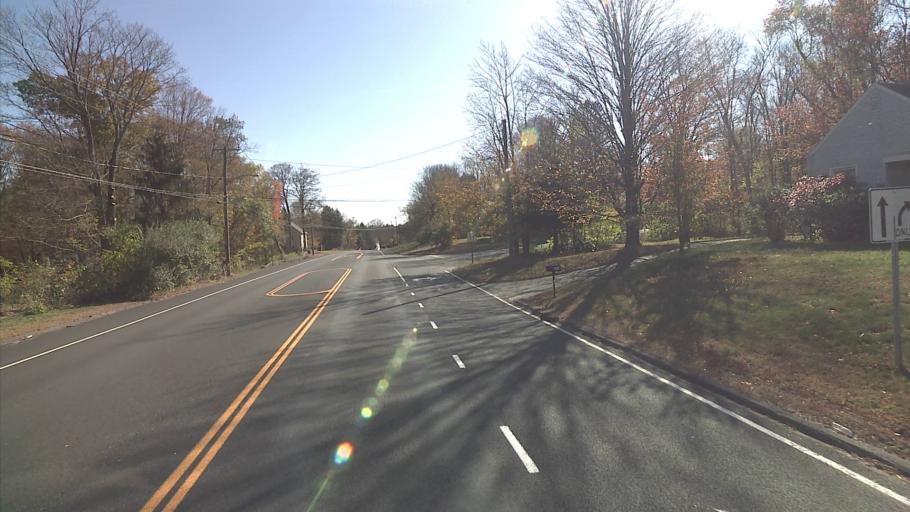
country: US
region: Connecticut
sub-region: Tolland County
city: Coventry Lake
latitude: 41.7469
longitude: -72.3896
